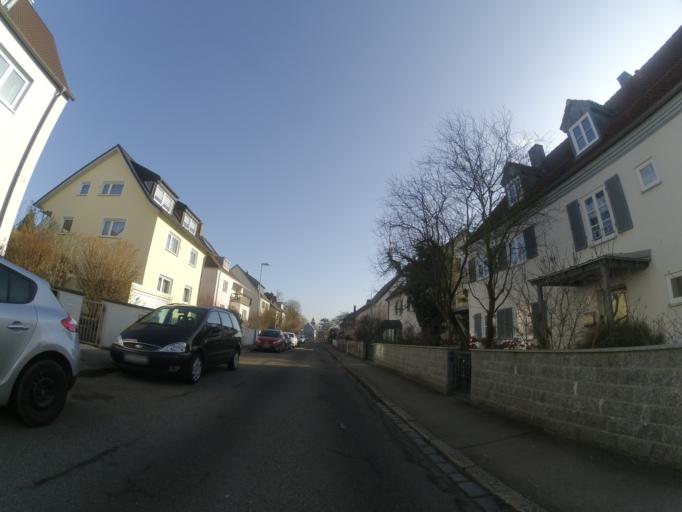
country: DE
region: Baden-Wuerttemberg
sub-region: Tuebingen Region
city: Ulm
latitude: 48.4128
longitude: 10.0001
